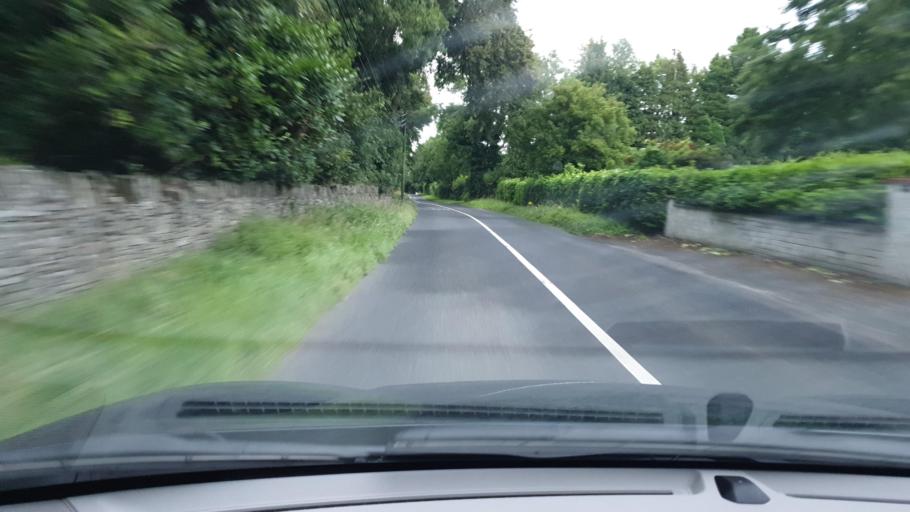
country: IE
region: Leinster
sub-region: South Dublin
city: Rathcoole
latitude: 53.2581
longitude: -6.4986
